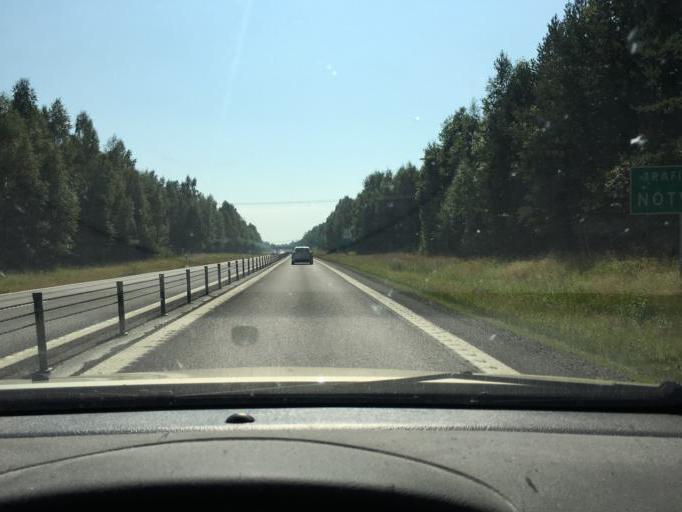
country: SE
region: Norrbotten
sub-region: Lulea Kommun
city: Gammelstad
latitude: 65.6330
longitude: 22.0632
